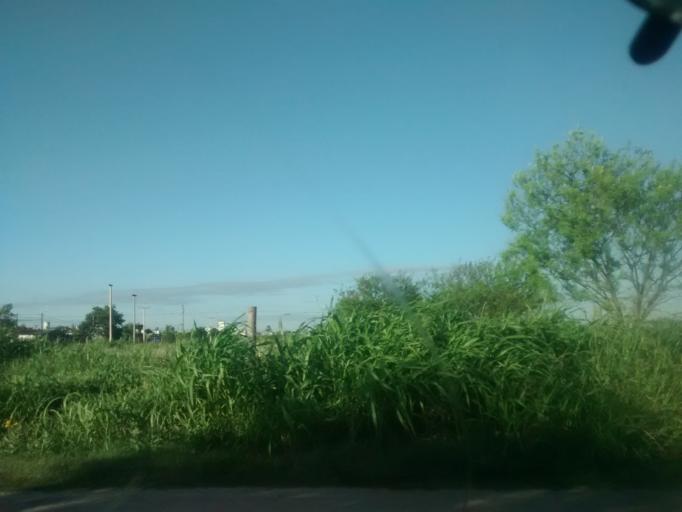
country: AR
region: Chaco
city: Fontana
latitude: -27.4510
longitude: -59.0257
